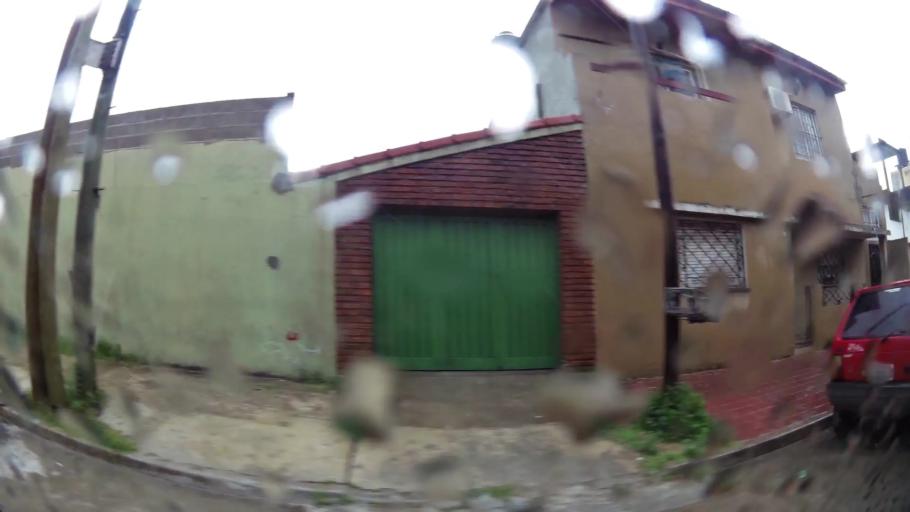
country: AR
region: Buenos Aires
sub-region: Partido de Lanus
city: Lanus
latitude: -34.7166
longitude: -58.4121
